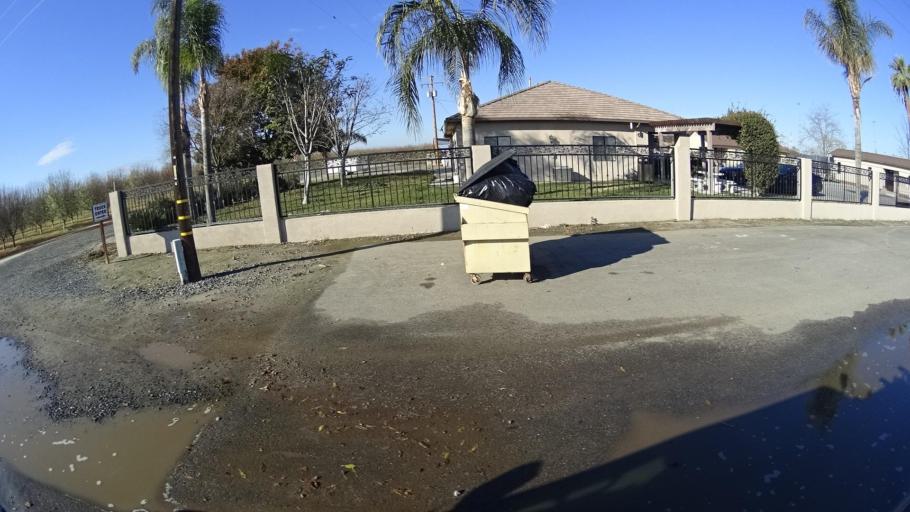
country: US
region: California
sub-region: Kern County
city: Delano
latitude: 35.7432
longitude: -119.2763
